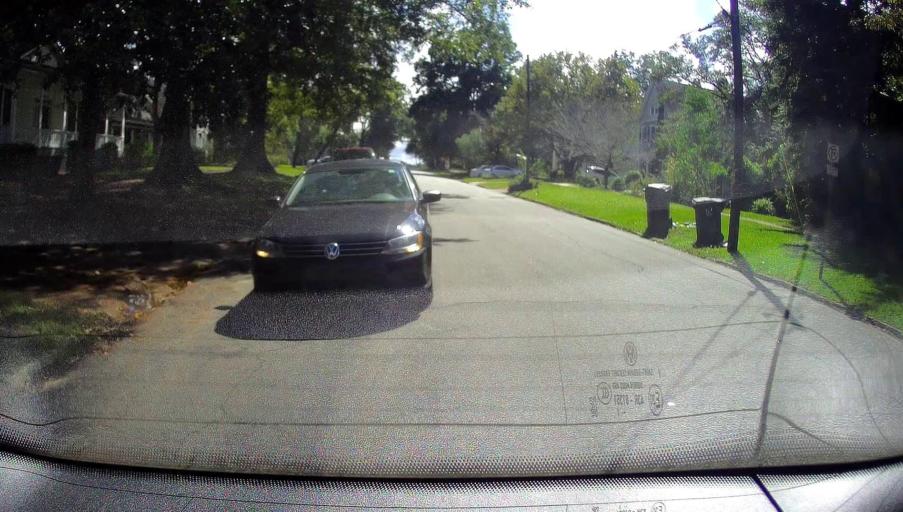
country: US
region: Georgia
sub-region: Baldwin County
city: Milledgeville
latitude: 33.0823
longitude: -83.2344
